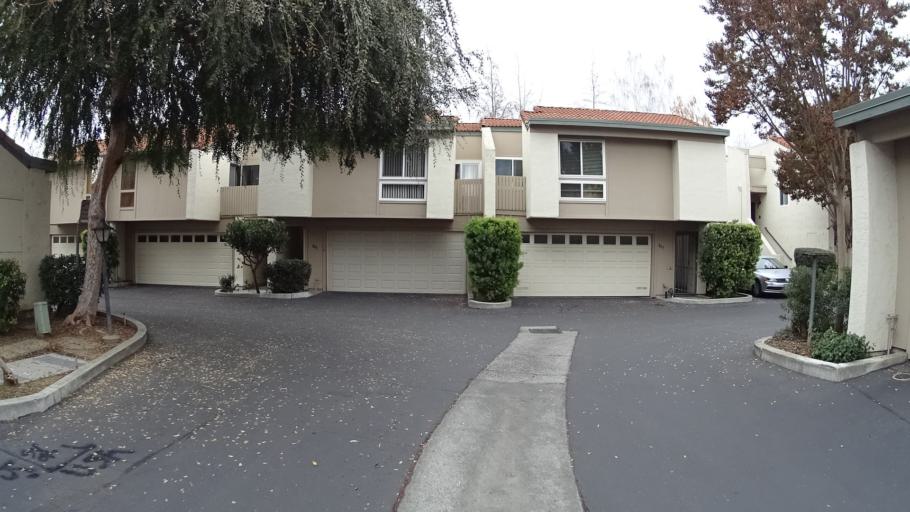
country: US
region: California
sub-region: Santa Clara County
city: Sunnyvale
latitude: 37.3532
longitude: -122.0169
